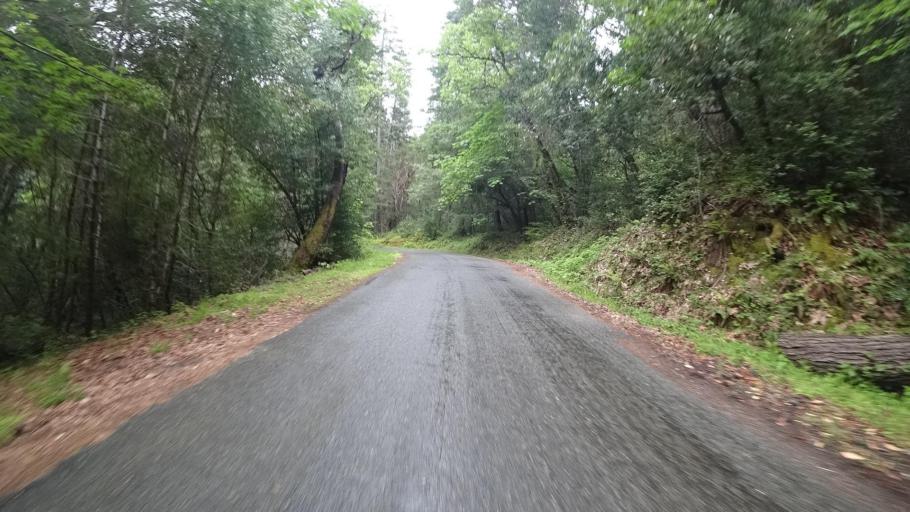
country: US
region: California
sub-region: Humboldt County
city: Willow Creek
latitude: 41.3652
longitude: -123.5062
